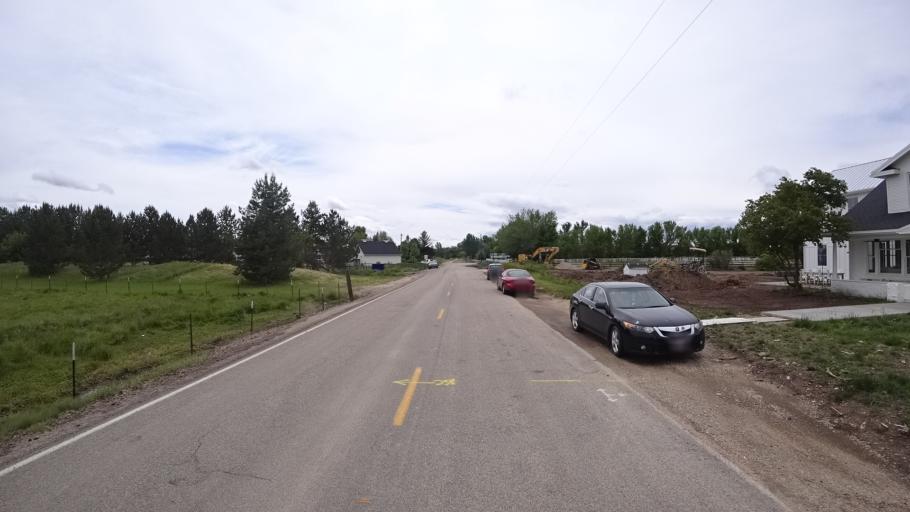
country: US
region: Idaho
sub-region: Ada County
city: Star
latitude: 43.6902
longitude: -116.4434
